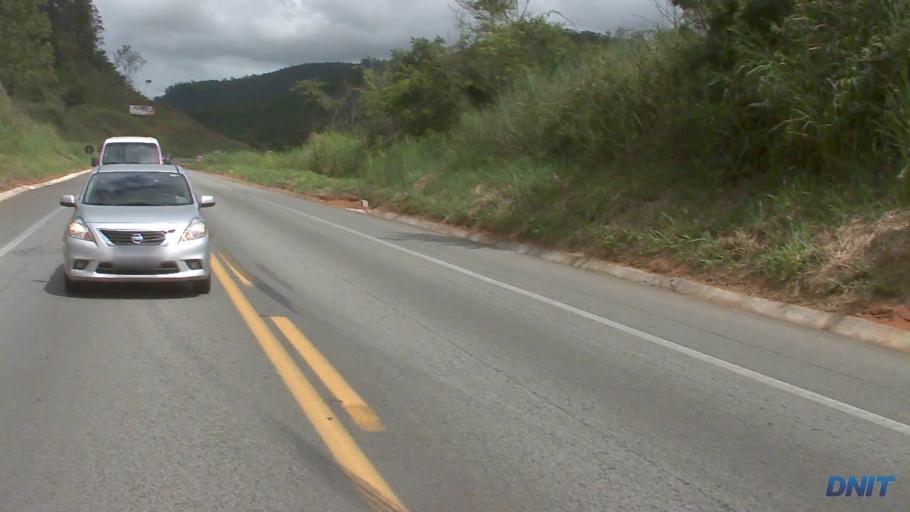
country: BR
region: Minas Gerais
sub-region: Joao Monlevade
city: Joao Monlevade
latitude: -19.8495
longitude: -43.1544
